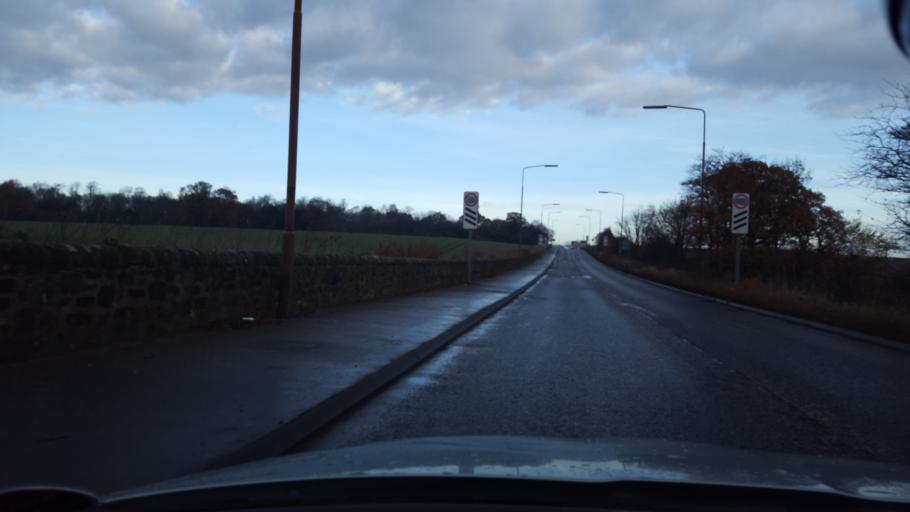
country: GB
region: Scotland
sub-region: Edinburgh
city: Queensferry
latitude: 55.9741
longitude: -3.3990
